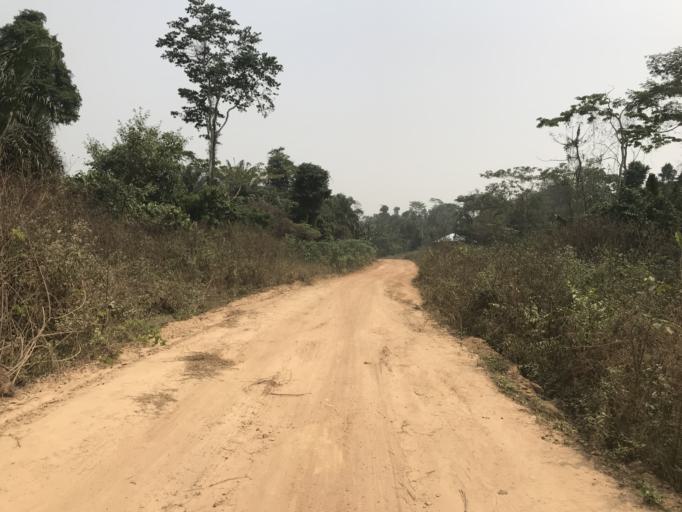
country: NG
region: Osun
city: Ifetedo
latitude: 7.0467
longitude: 4.4663
